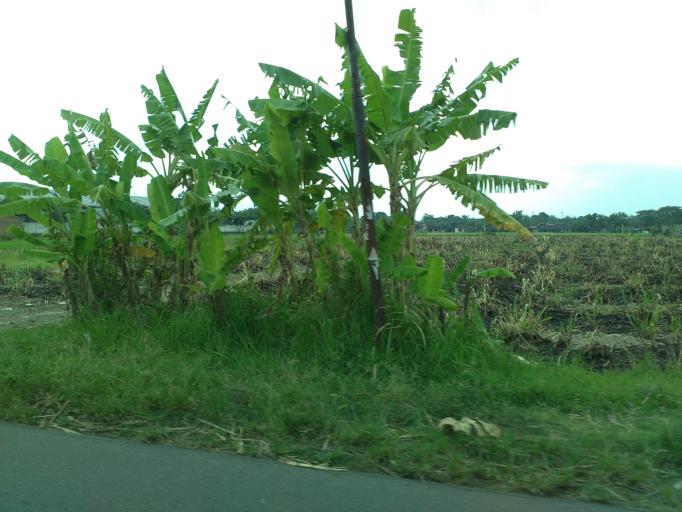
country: ID
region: Central Java
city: Ceper
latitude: -7.6634
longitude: 110.6635
